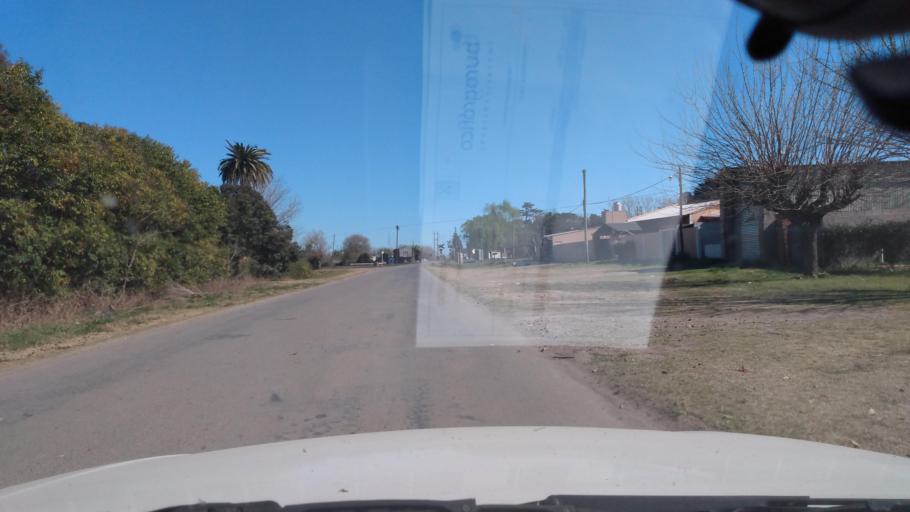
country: AR
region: Buenos Aires
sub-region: Partido de Mercedes
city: Mercedes
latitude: -34.6589
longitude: -59.4029
